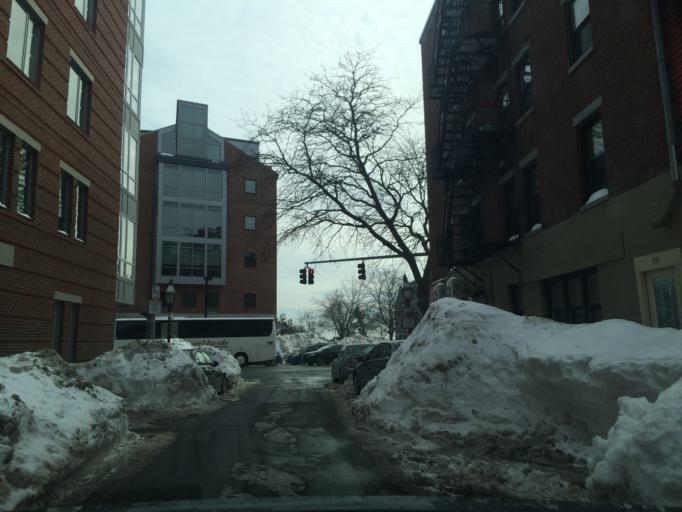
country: US
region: Massachusetts
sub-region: Suffolk County
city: Boston
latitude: 42.3642
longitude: -71.0516
